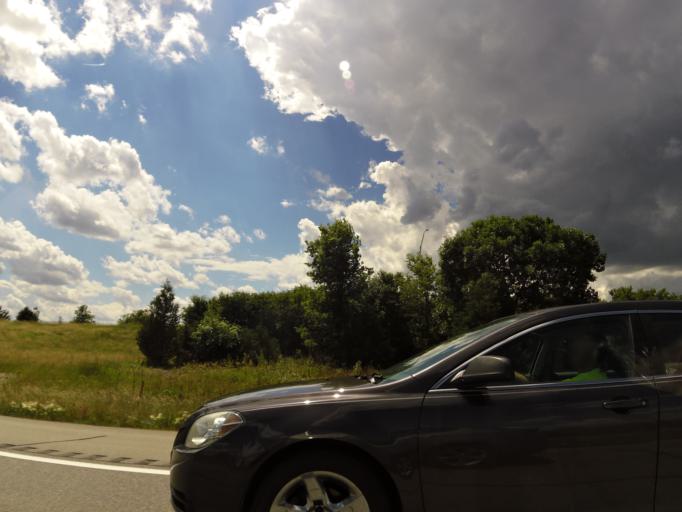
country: US
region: Iowa
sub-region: Linn County
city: Robins
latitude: 42.0920
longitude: -91.7016
